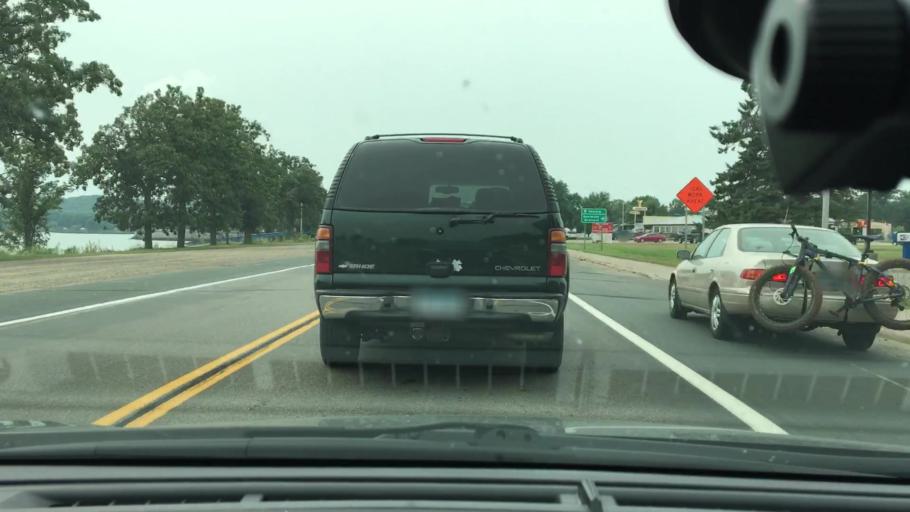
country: US
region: Minnesota
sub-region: Mille Lacs County
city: Vineland
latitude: 46.2971
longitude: -93.8229
